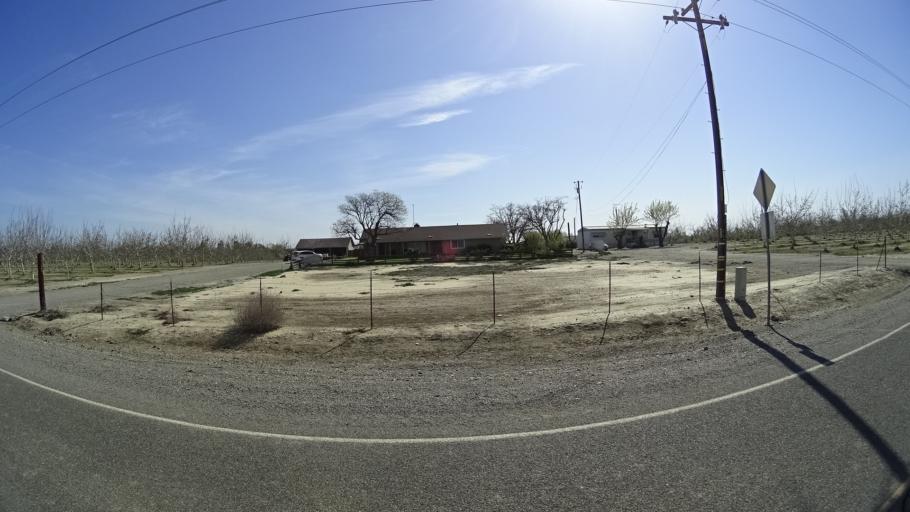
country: US
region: California
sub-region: Glenn County
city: Willows
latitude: 39.5517
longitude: -122.1652
